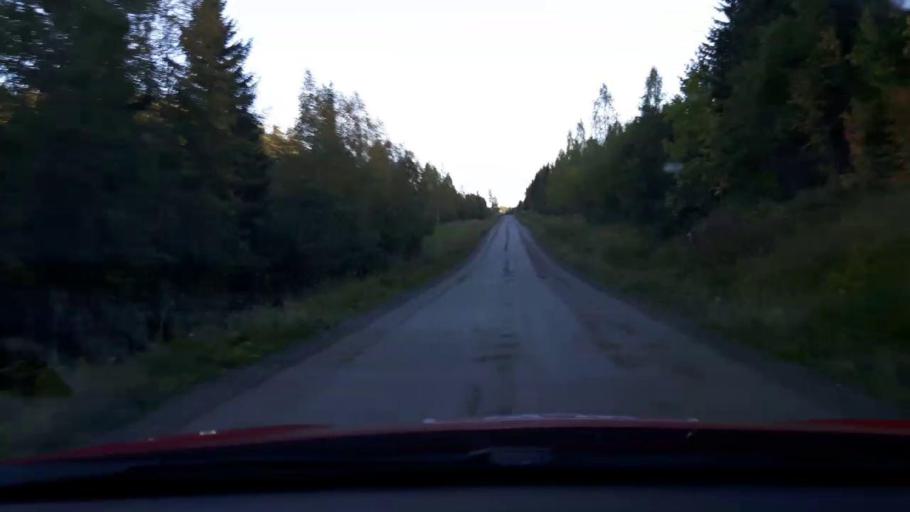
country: SE
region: Jaemtland
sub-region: OEstersunds Kommun
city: Brunflo
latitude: 62.9376
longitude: 14.9923
